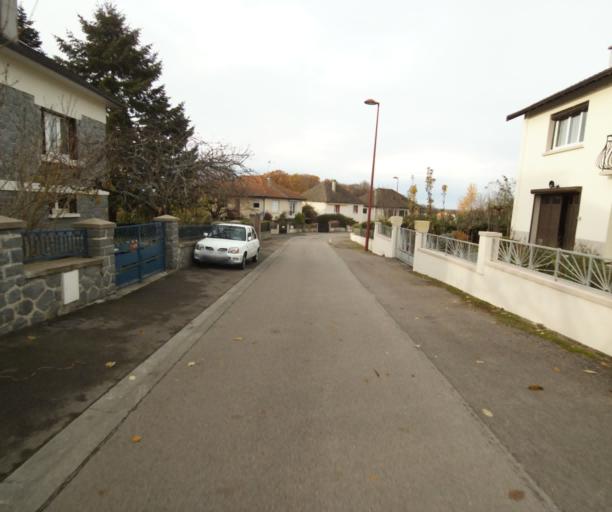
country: FR
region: Limousin
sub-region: Departement de la Correze
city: Sainte-Fortunade
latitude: 45.2135
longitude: 1.7685
